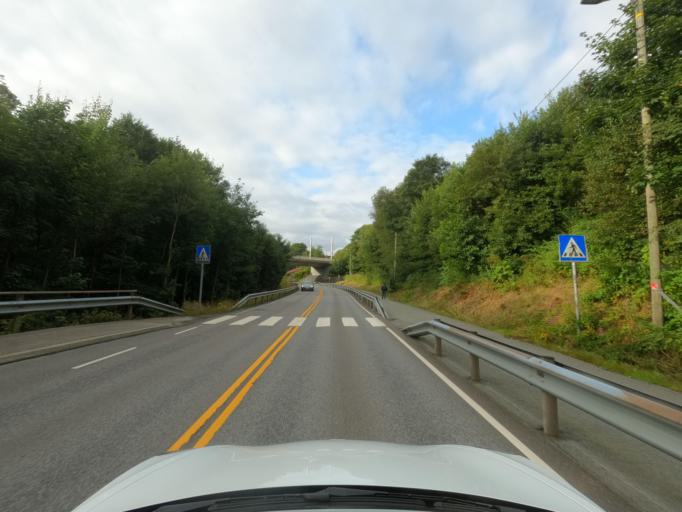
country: NO
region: Hordaland
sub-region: Bergen
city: Sandsli
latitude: 60.3008
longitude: 5.2983
